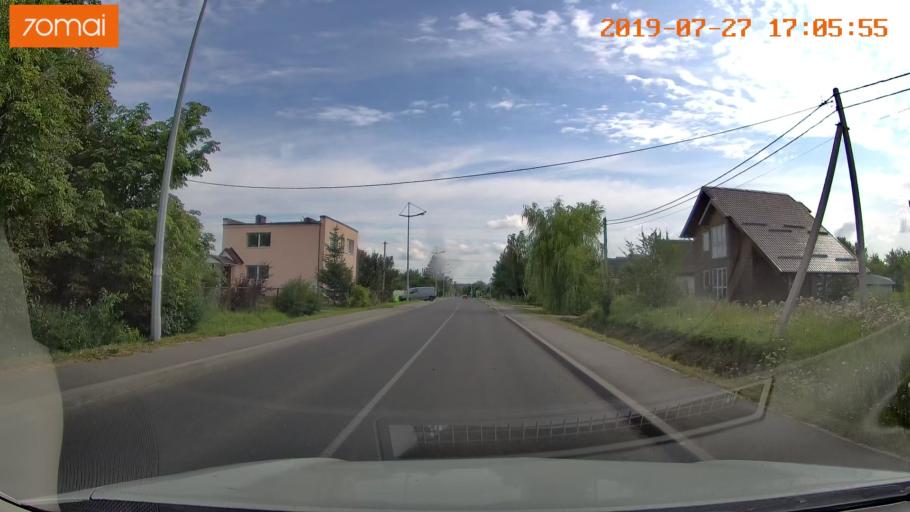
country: RU
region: Kaliningrad
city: Bol'shoe Isakovo
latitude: 54.7248
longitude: 20.6018
